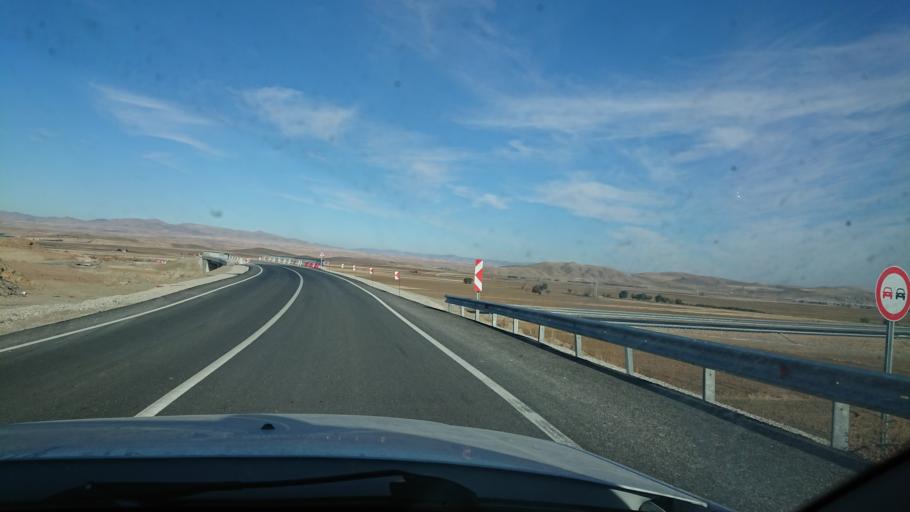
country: TR
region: Aksaray
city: Sariyahsi
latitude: 38.9979
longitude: 33.8526
